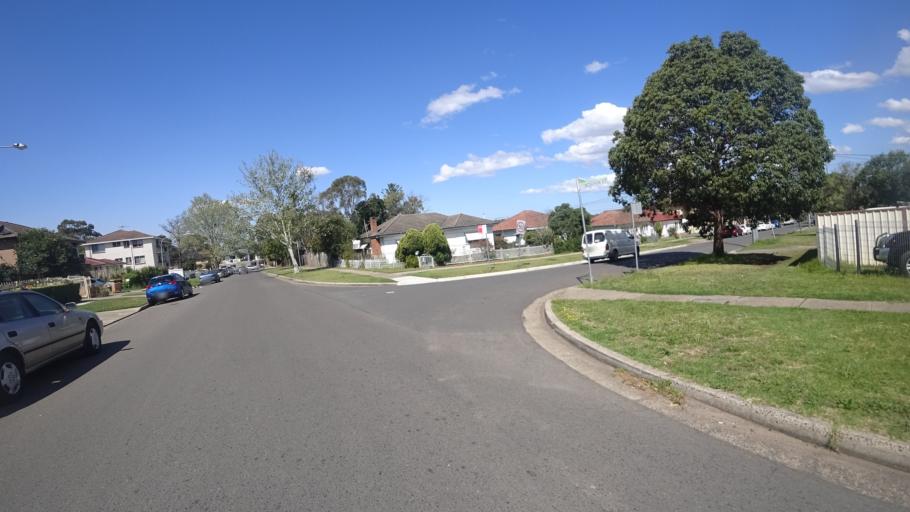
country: AU
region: New South Wales
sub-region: Fairfield
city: Liverpool
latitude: -33.8980
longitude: 150.9353
